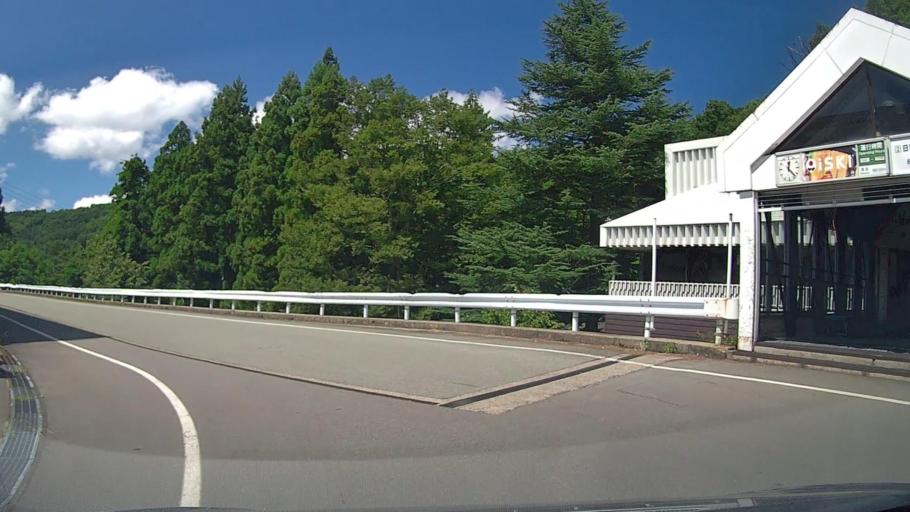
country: JP
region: Nagano
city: Iiyama
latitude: 36.9256
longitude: 138.4532
